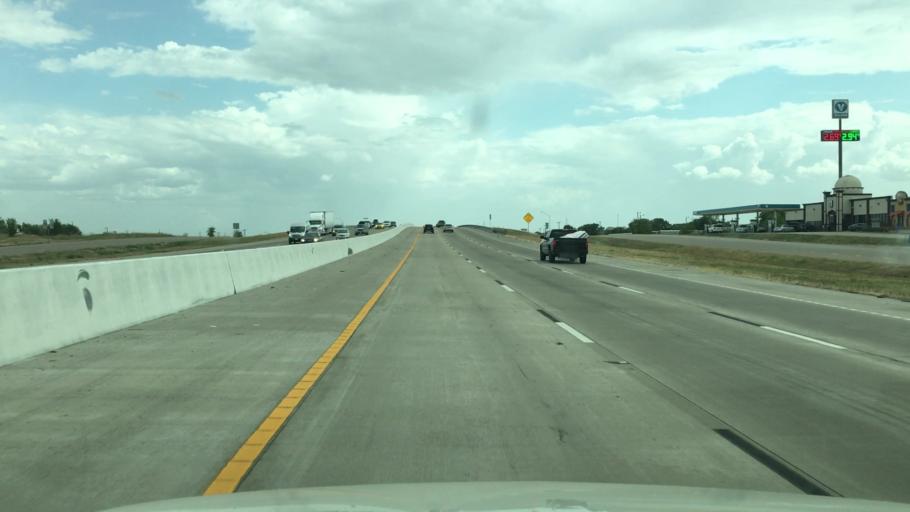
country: US
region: Texas
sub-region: McLennan County
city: Northcrest
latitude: 31.7196
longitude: -97.1027
